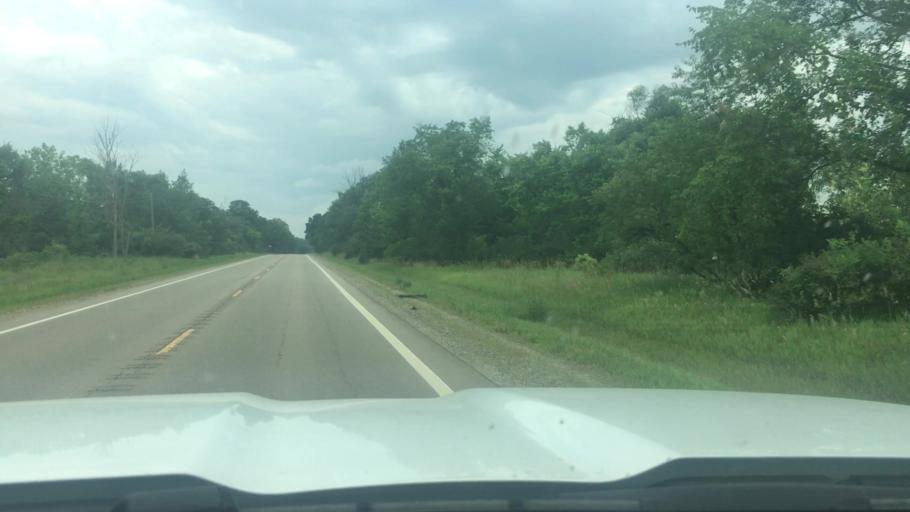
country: US
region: Michigan
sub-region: Ionia County
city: Portland
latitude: 43.0012
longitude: -84.8979
